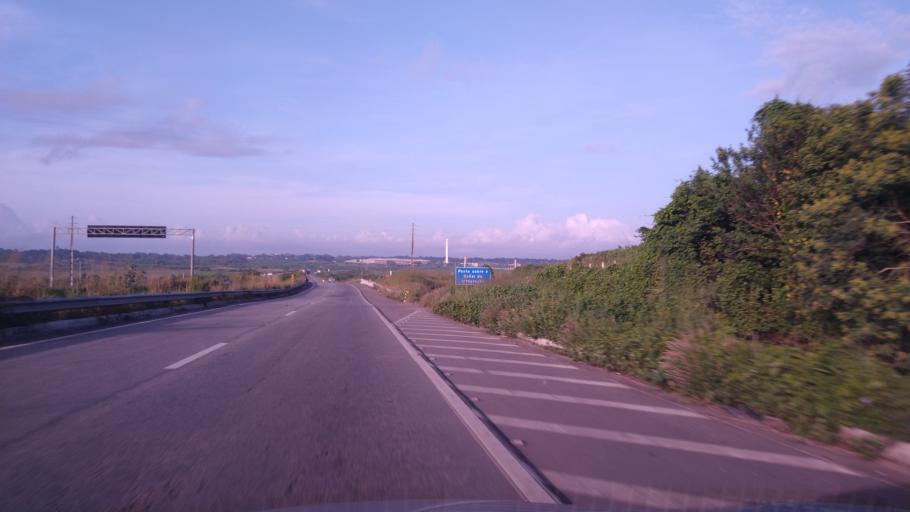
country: BR
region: Ceara
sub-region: Pacajus
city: Pacajus
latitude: -4.1544
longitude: -38.4811
